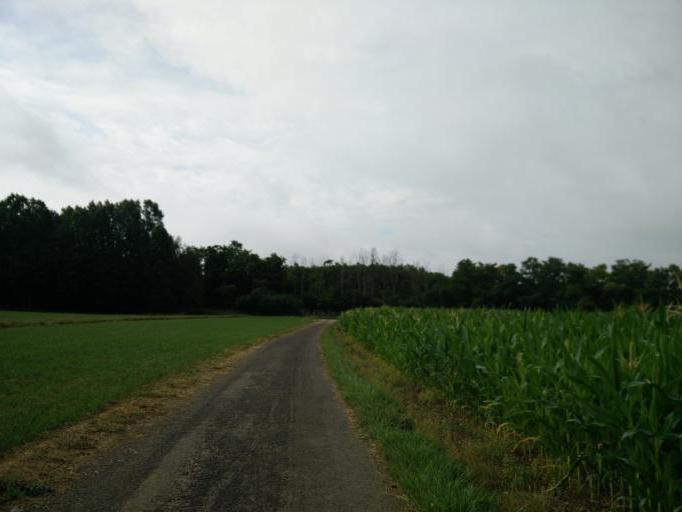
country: LU
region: Luxembourg
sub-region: Canton de Capellen
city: Mamer
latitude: 49.6325
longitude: 6.0421
